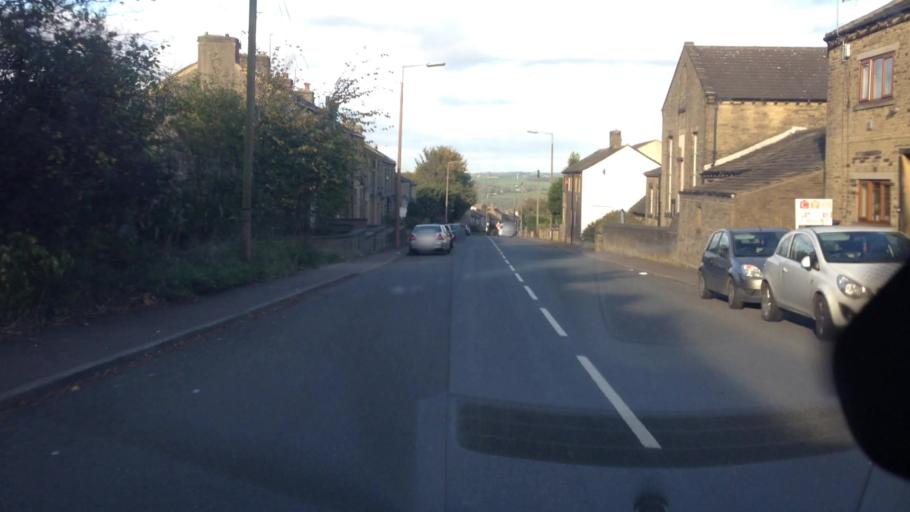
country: GB
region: England
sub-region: Calderdale
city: Brighouse
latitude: 53.6833
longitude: -1.7999
